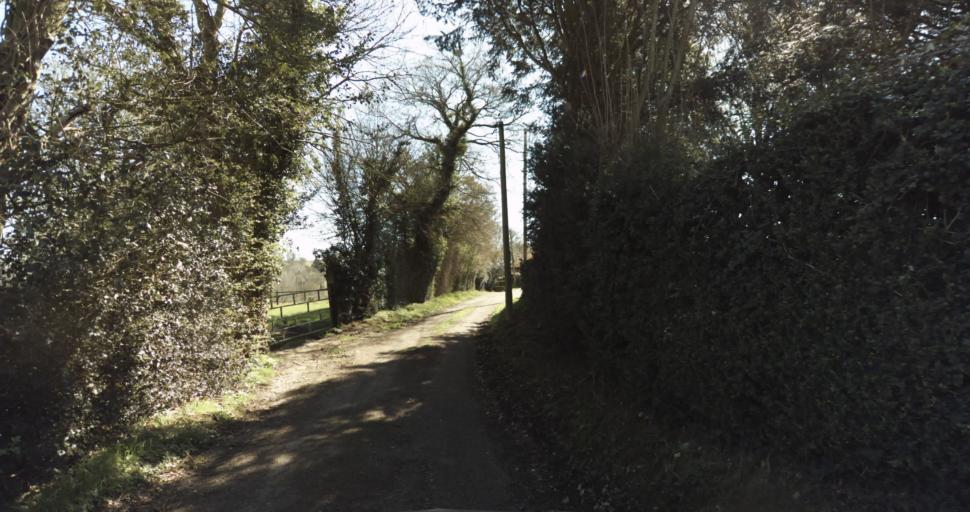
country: FR
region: Lower Normandy
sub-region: Departement du Calvados
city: Livarot
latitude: 48.9866
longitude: 0.0937
